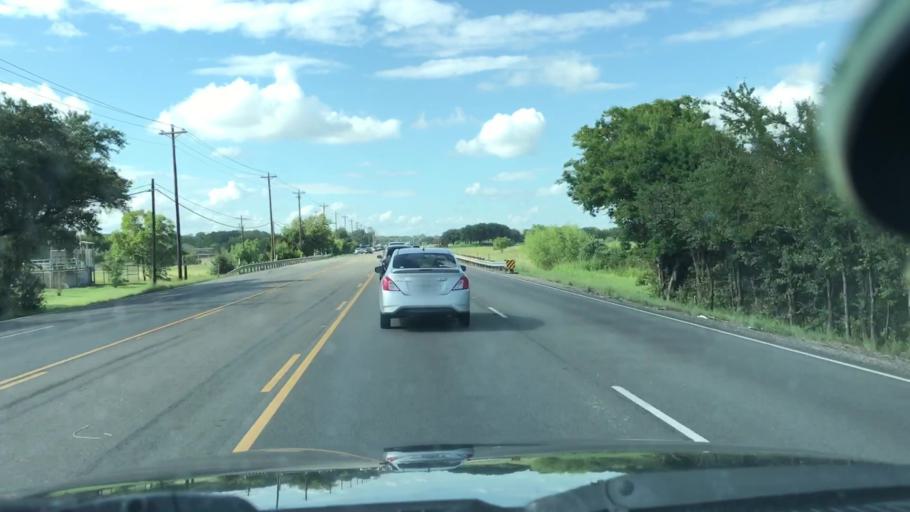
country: US
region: Texas
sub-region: Williamson County
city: Cedar Park
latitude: 30.5388
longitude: -97.8376
